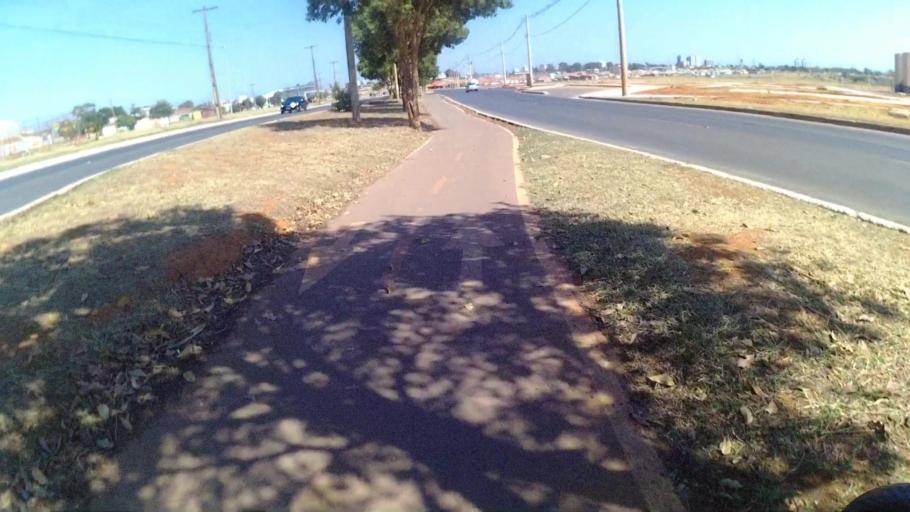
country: BR
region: Federal District
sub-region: Brasilia
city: Brasilia
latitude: -15.8915
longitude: -48.0490
